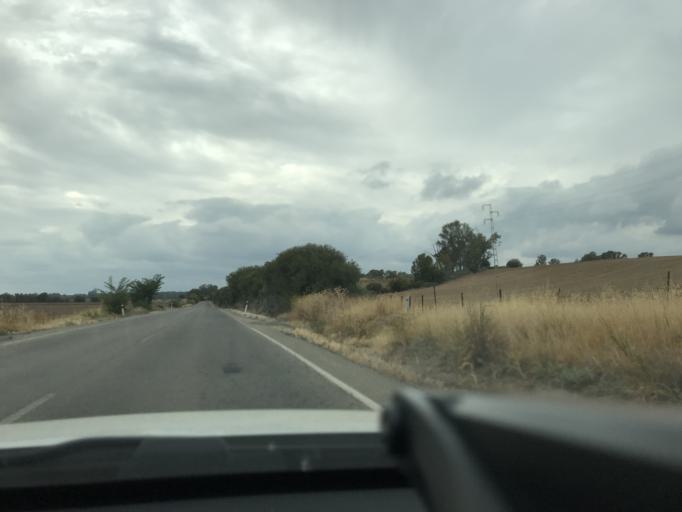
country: ES
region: Andalusia
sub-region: Provincia de Sevilla
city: Villanueva del Rio y Minas
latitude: 37.6353
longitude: -5.7211
